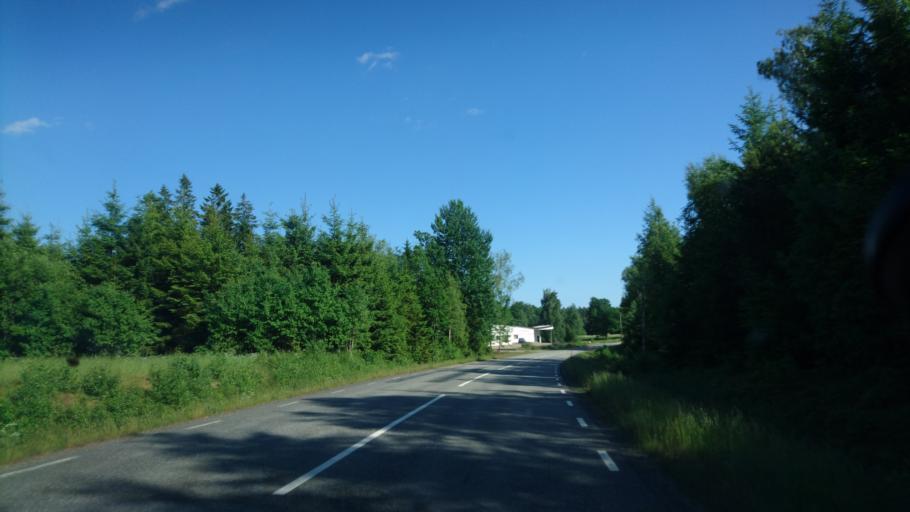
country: SE
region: Skane
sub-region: Osby Kommun
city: Lonsboda
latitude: 56.4236
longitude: 14.2820
